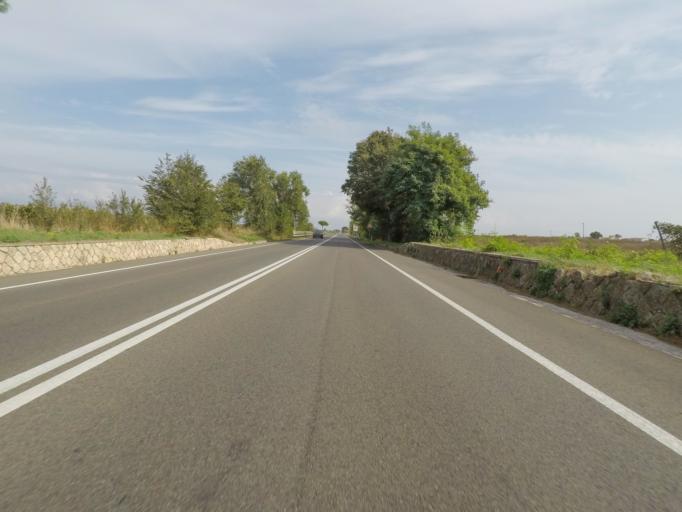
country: IT
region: Tuscany
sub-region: Provincia di Grosseto
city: Capalbio
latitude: 42.4146
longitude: 11.4184
